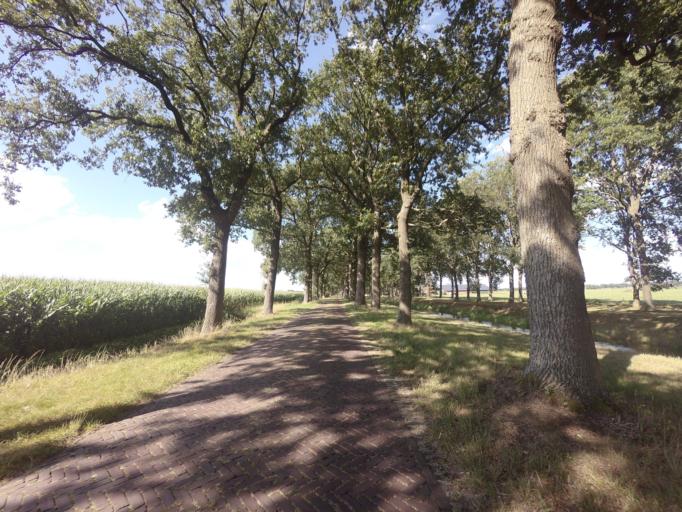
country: NL
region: Drenthe
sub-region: Gemeente Hoogeveen
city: Hoogeveen
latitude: 52.6595
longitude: 6.5147
